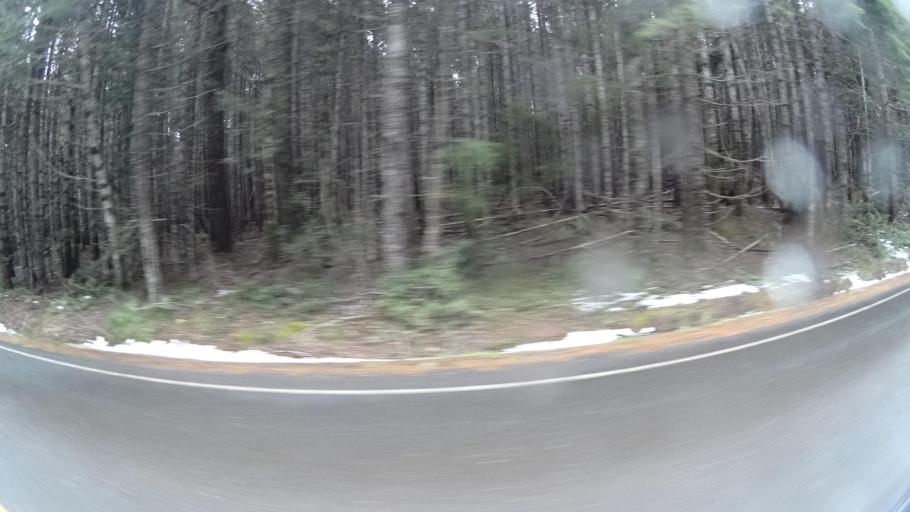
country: US
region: California
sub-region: Humboldt County
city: Willow Creek
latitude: 41.1797
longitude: -123.8159
